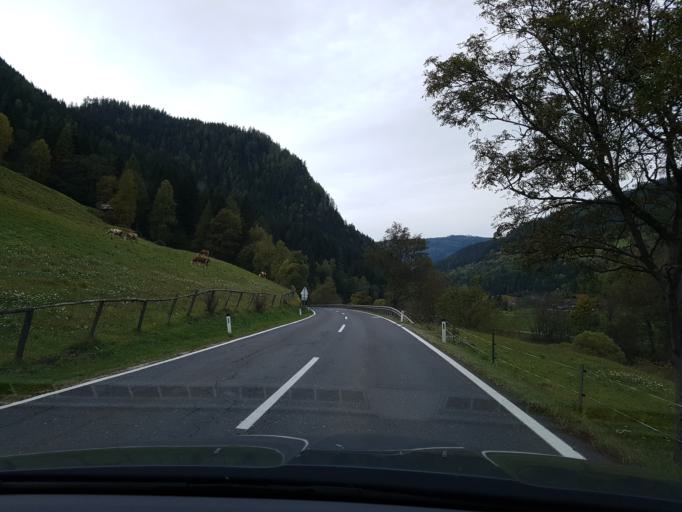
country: AT
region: Salzburg
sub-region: Politischer Bezirk Tamsweg
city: Ramingstein
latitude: 47.0732
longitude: 13.8590
